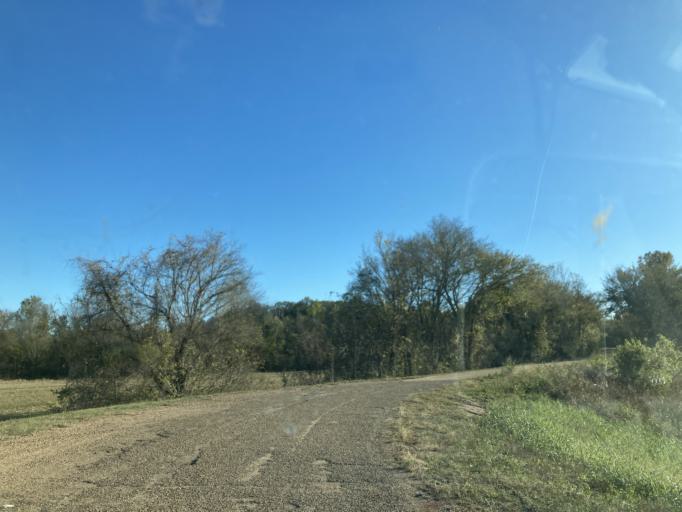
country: US
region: Mississippi
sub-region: Yazoo County
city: Yazoo City
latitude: 32.7529
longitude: -90.4870
